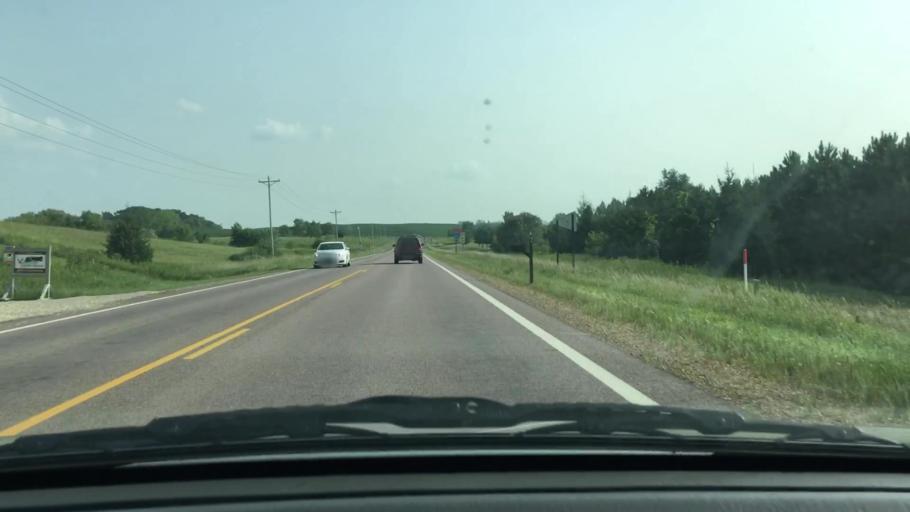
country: US
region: Minnesota
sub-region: Scott County
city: Elko New Market
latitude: 44.5491
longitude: -93.3395
